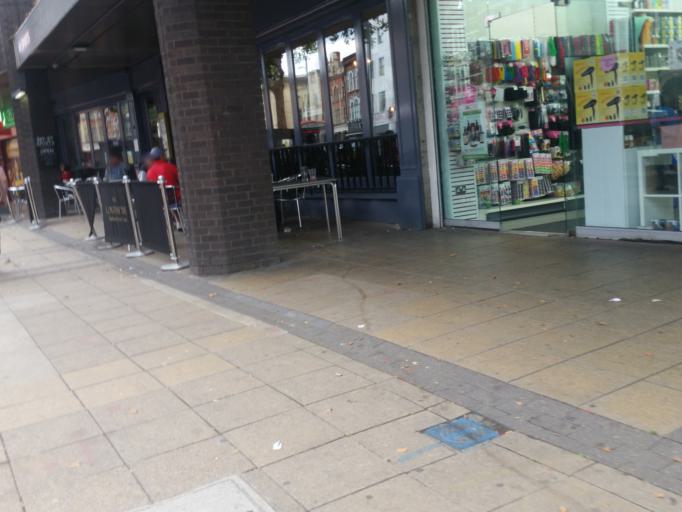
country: GB
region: England
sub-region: Greater London
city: Poplar
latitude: 51.5404
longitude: 0.0004
